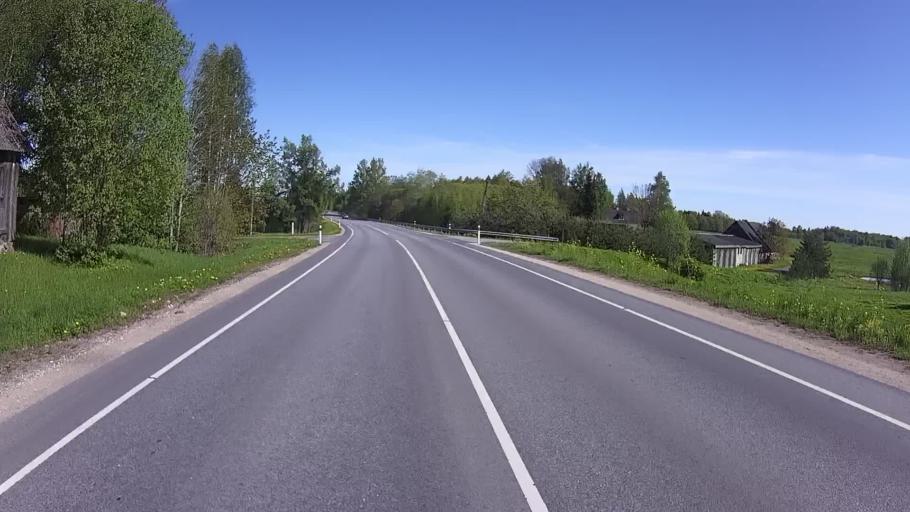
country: EE
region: Polvamaa
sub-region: Polva linn
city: Polva
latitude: 58.2659
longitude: 27.0054
